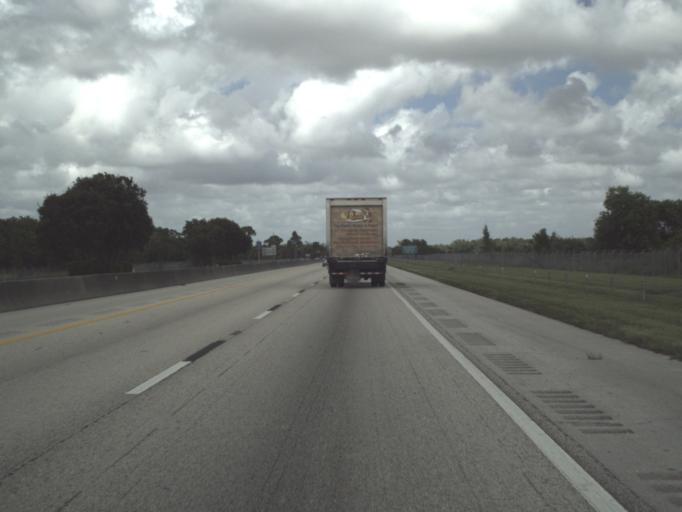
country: US
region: Florida
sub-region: Palm Beach County
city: Lake Belvedere Estates
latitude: 26.6535
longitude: -80.1741
